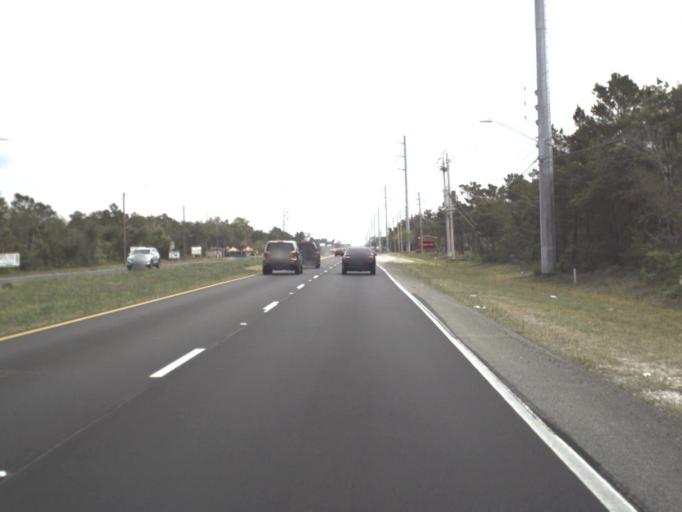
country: US
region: Florida
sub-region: Santa Rosa County
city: Woodlawn Beach
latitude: 30.3977
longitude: -87.0135
